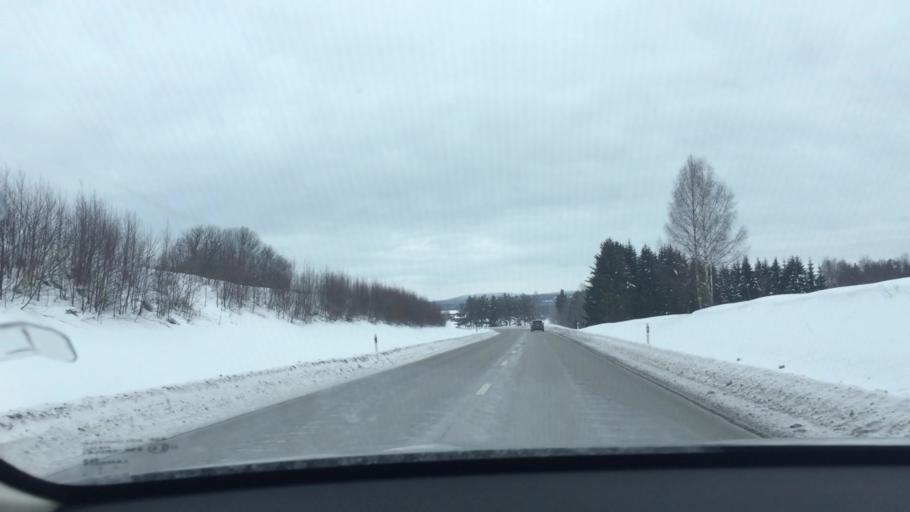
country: SE
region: Dalarna
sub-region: Faluns Kommun
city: Svardsjo
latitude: 60.6273
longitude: 15.8250
